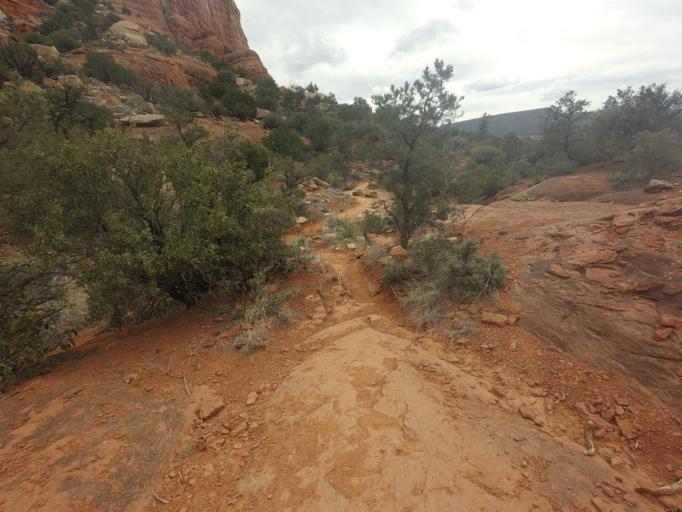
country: US
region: Arizona
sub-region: Yavapai County
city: Village of Oak Creek (Big Park)
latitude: 34.8019
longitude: -111.7611
